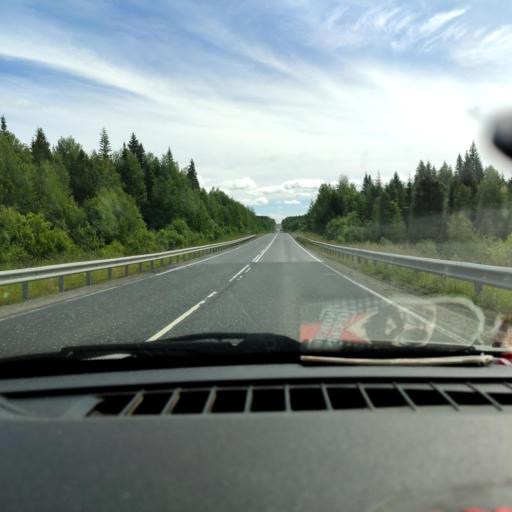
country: RU
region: Perm
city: Chusovoy
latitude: 58.3739
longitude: 57.9766
